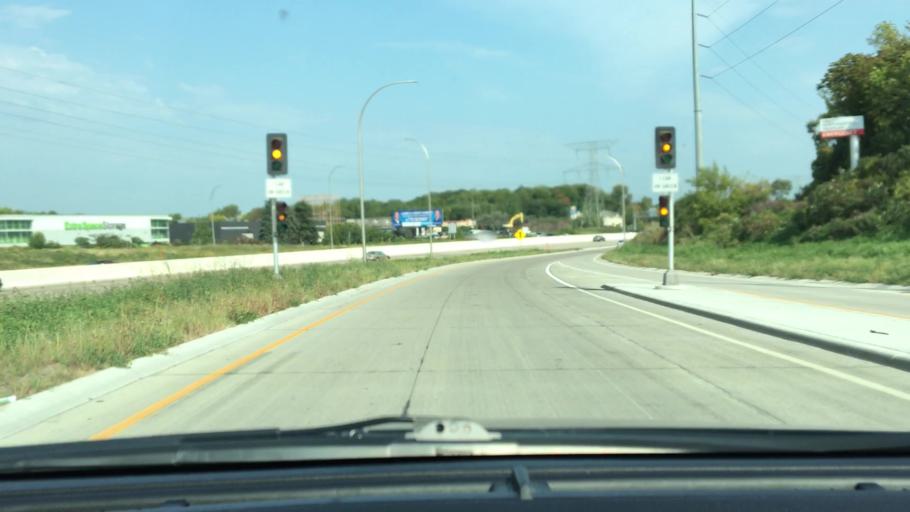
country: US
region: Minnesota
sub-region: Hennepin County
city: Plymouth
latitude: 45.0121
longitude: -93.4565
